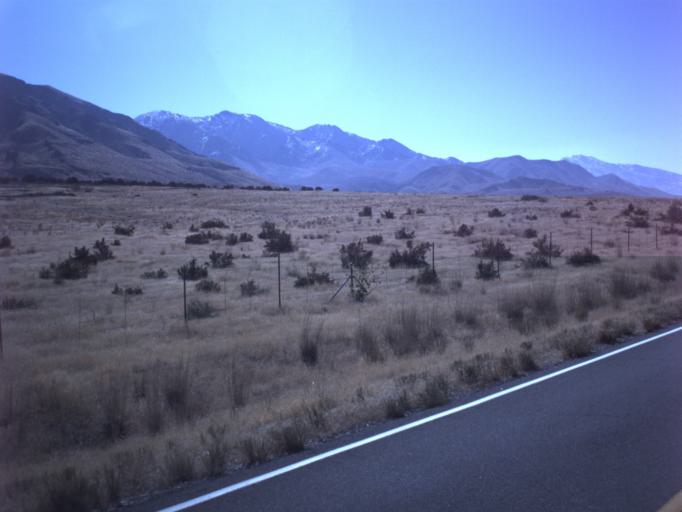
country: US
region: Utah
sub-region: Tooele County
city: Grantsville
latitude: 40.6728
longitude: -112.6734
